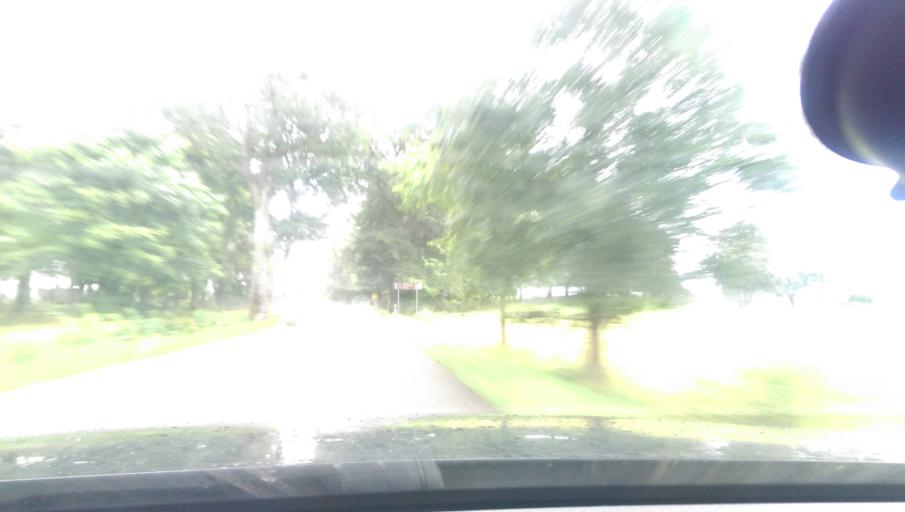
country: PL
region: Warmian-Masurian Voivodeship
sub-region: Powiat piski
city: Ruciane-Nida
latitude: 53.6935
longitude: 21.4787
